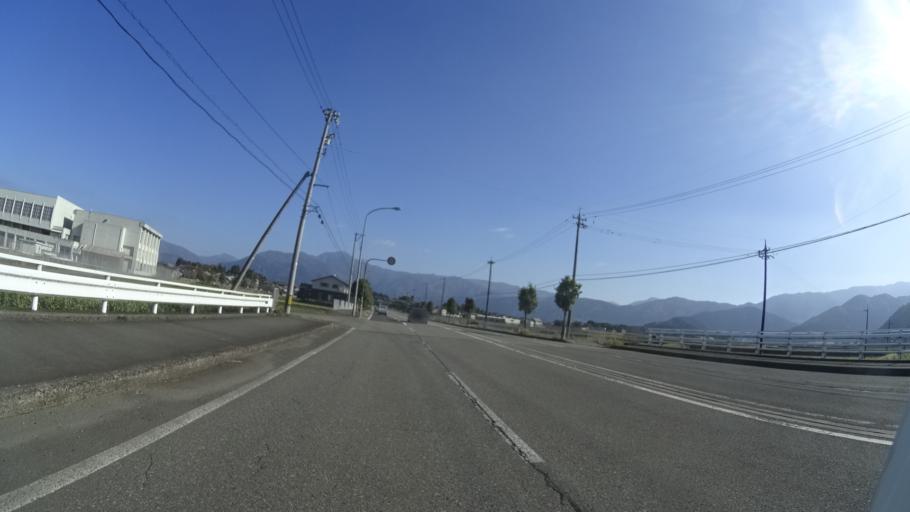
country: JP
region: Fukui
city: Ono
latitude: 35.9722
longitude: 136.4820
